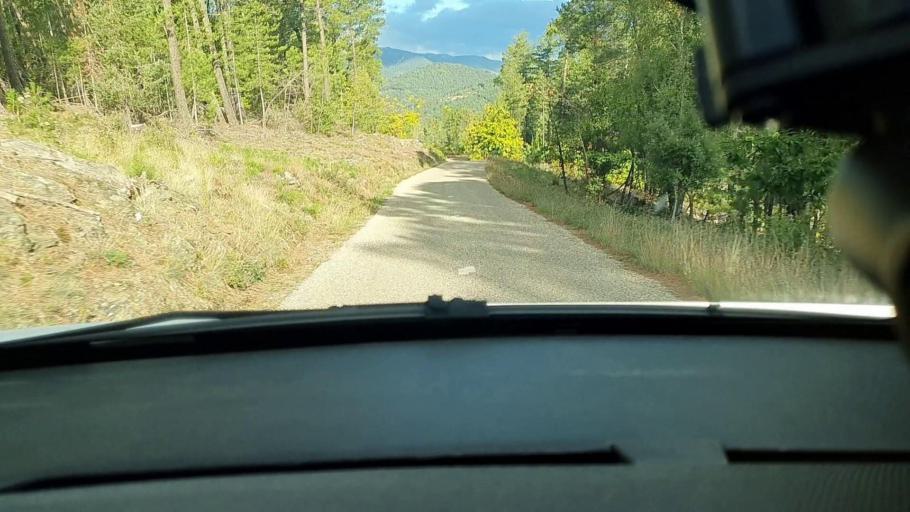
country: FR
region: Languedoc-Roussillon
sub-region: Departement du Gard
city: Besseges
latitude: 44.3437
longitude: 3.9861
